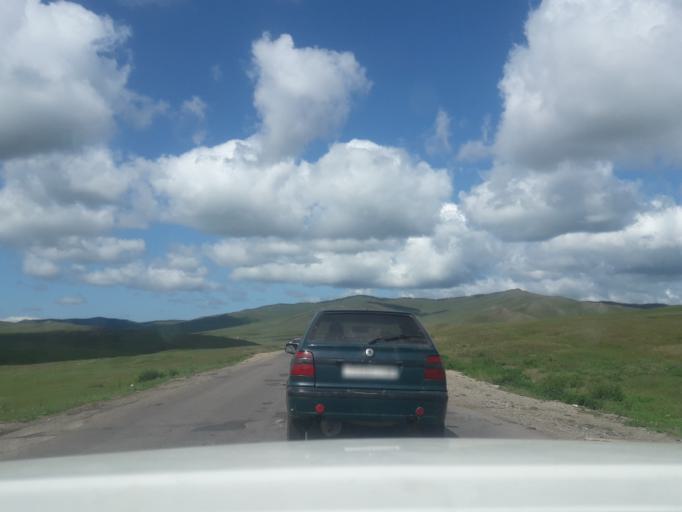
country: MN
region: Central Aimak
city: Ihsueuej
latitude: 48.1571
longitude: 106.4060
